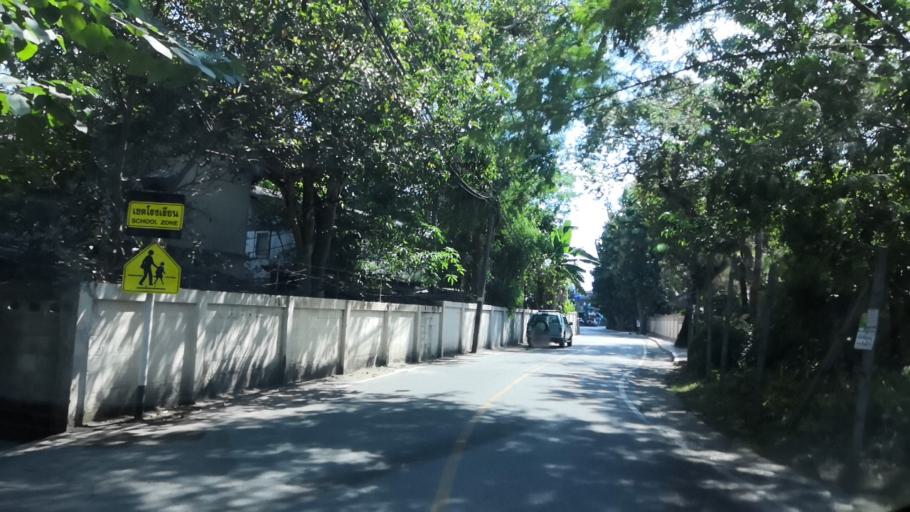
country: TH
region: Chiang Mai
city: Chiang Mai
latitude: 18.8113
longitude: 98.9700
